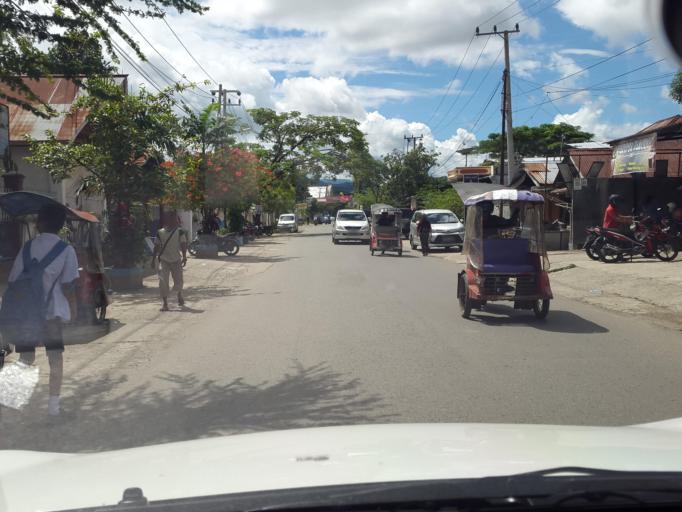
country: ID
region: South Sulawesi
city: Rantepao
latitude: -2.9734
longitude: 119.8954
